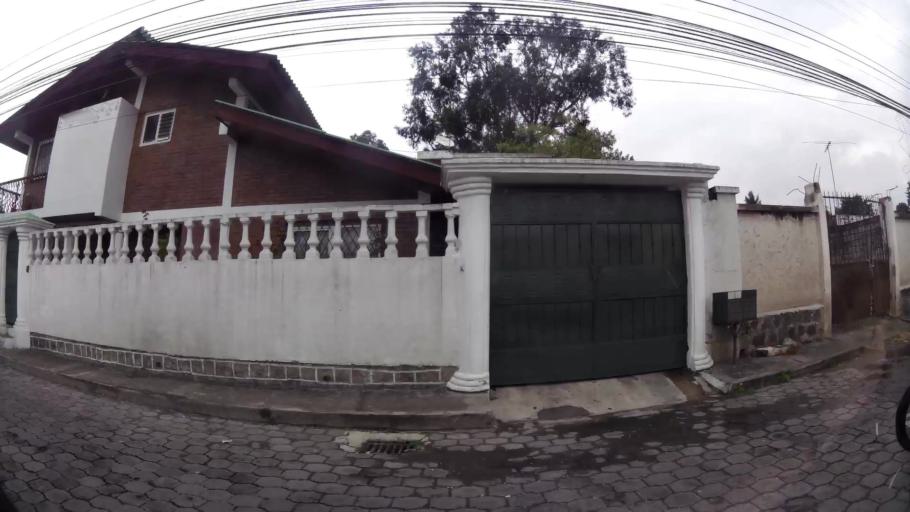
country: EC
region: Pichincha
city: Sangolqui
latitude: -0.2987
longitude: -78.4723
